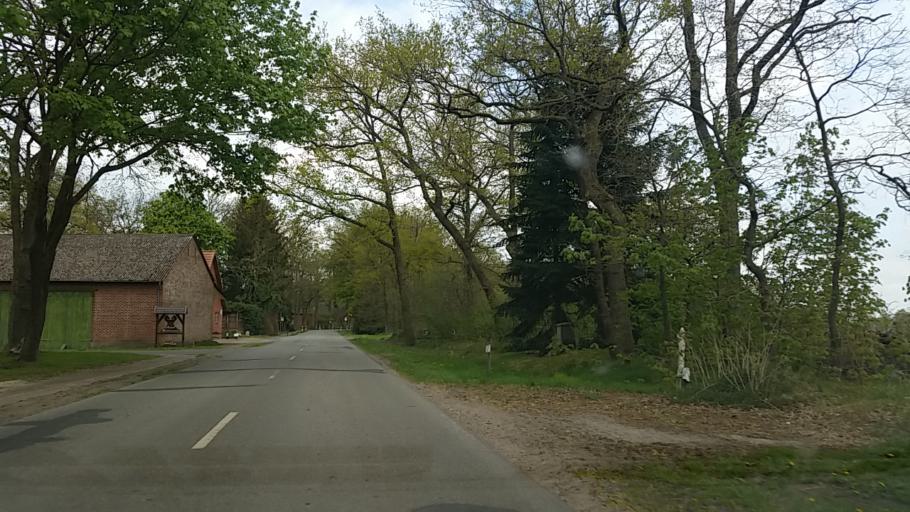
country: DE
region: Lower Saxony
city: Konigsmoor
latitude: 53.2008
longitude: 9.7067
